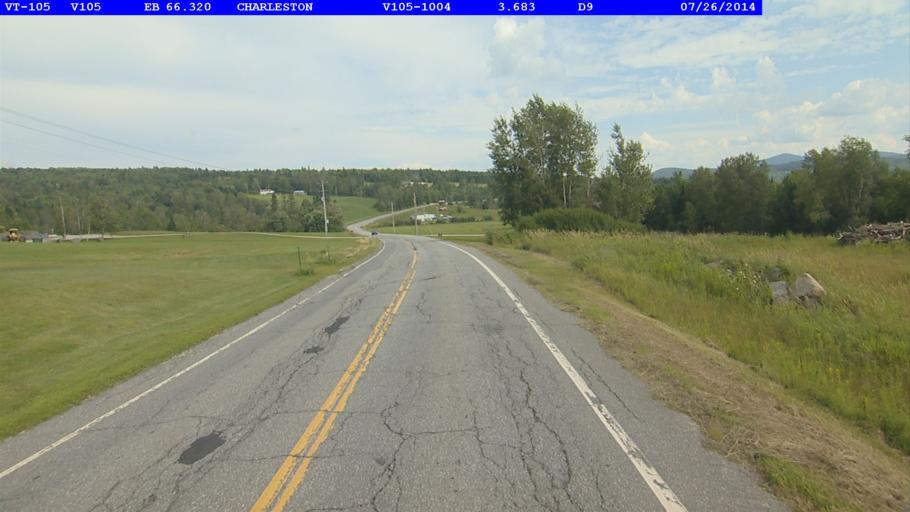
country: US
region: Vermont
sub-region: Orleans County
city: Newport
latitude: 44.8649
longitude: -72.0433
